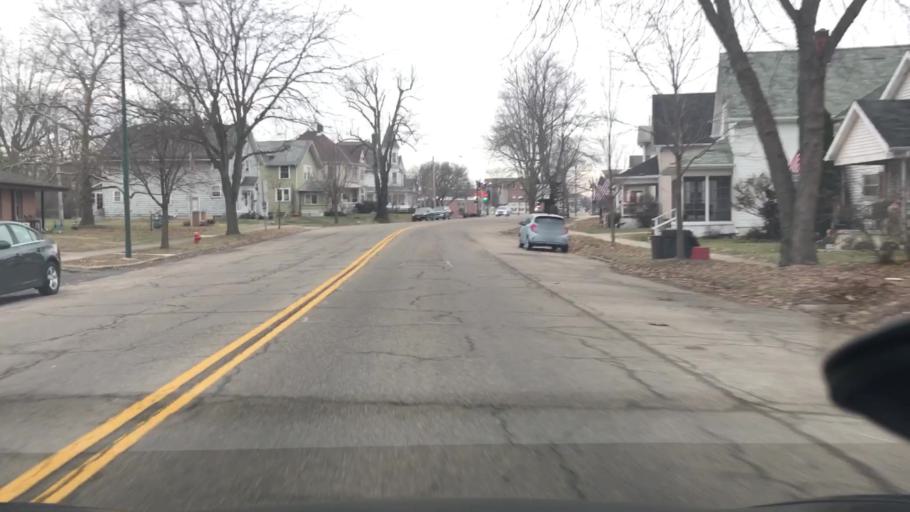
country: US
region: Ohio
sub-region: Madison County
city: London
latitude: 39.8819
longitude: -83.4432
